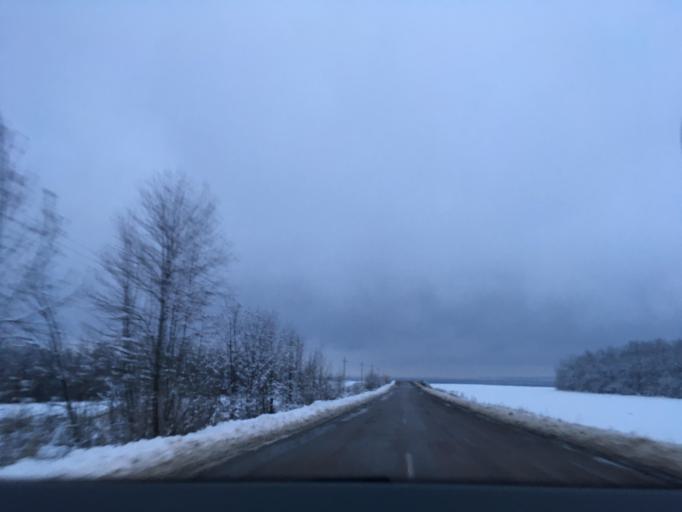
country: RU
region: Voronezj
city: Verkhniy Mamon
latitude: 50.0686
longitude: 40.2846
